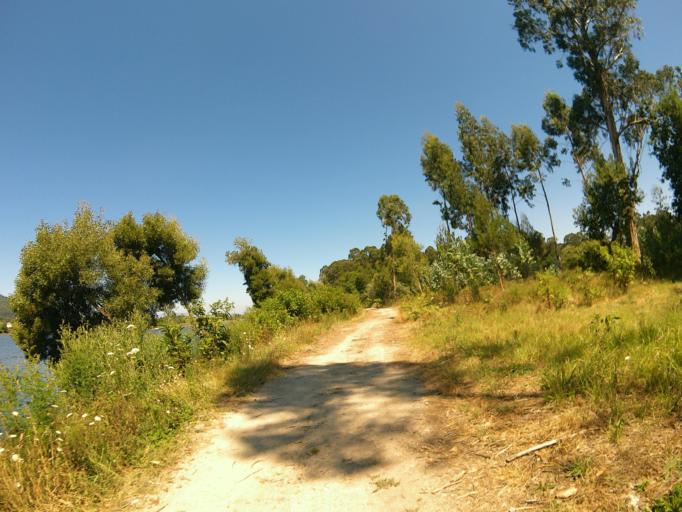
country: PT
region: Viana do Castelo
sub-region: Viana do Castelo
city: Darque
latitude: 41.6962
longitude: -8.7580
